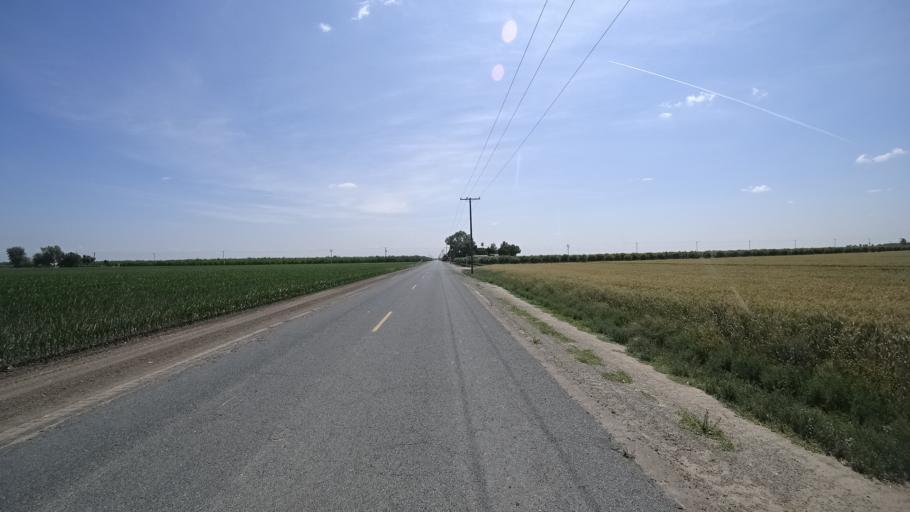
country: US
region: California
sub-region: Tulare County
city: Goshen
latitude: 36.2691
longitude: -119.4958
